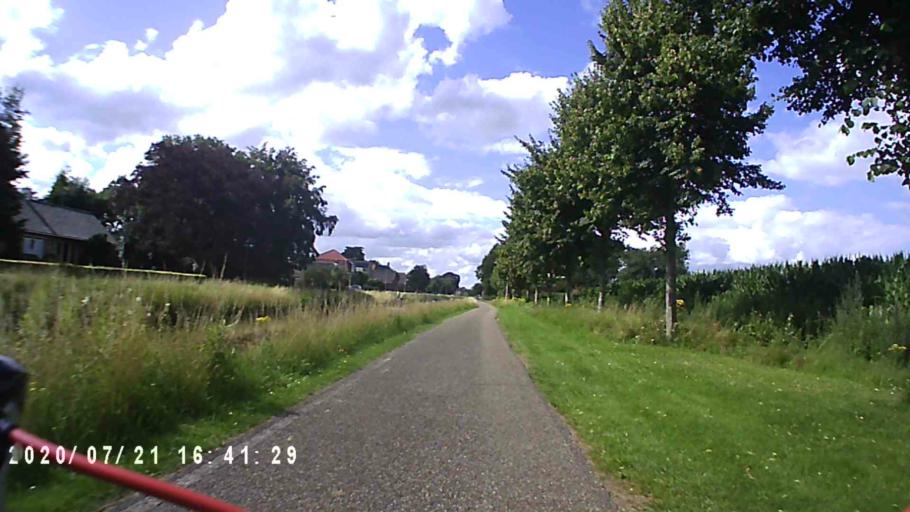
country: NL
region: Groningen
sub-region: Gemeente Hoogezand-Sappemeer
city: Sappemeer
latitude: 53.1010
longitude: 6.7881
